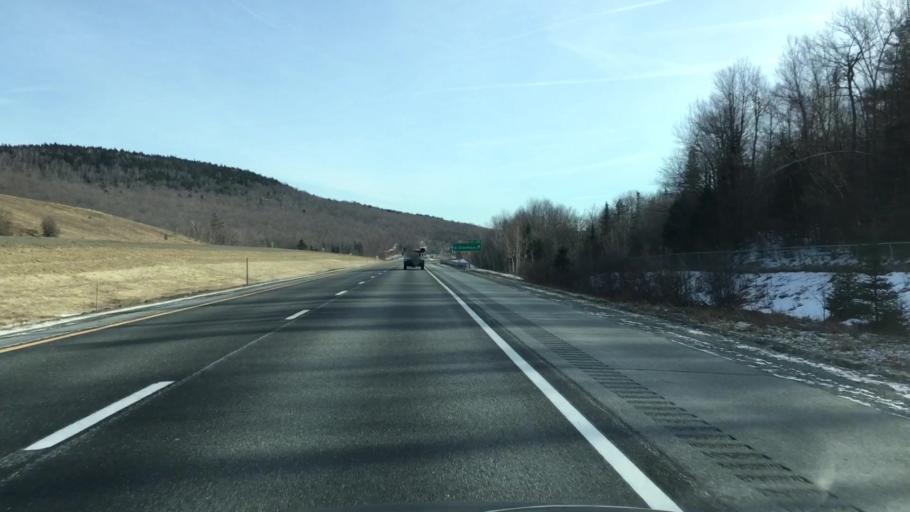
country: US
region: New Hampshire
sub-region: Grafton County
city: Enfield
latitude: 43.5702
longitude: -72.1546
